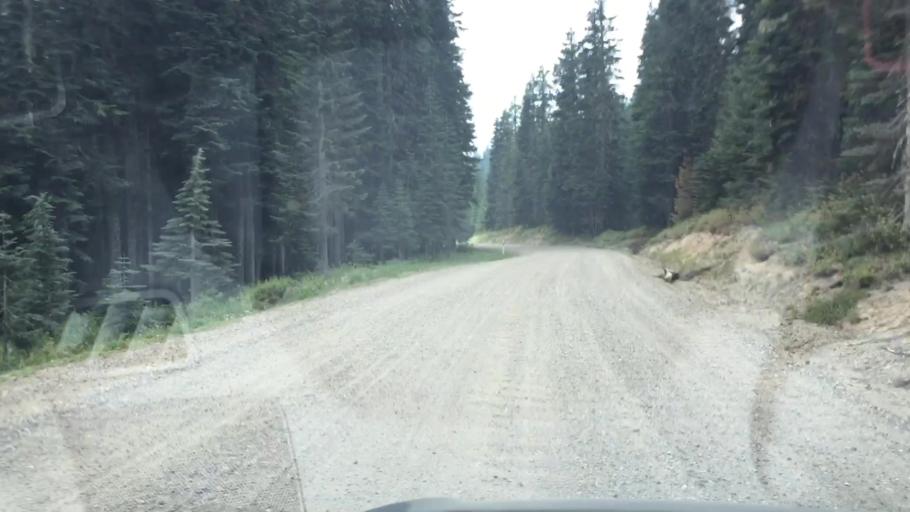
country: US
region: Washington
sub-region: Klickitat County
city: White Salmon
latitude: 46.2671
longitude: -121.6058
